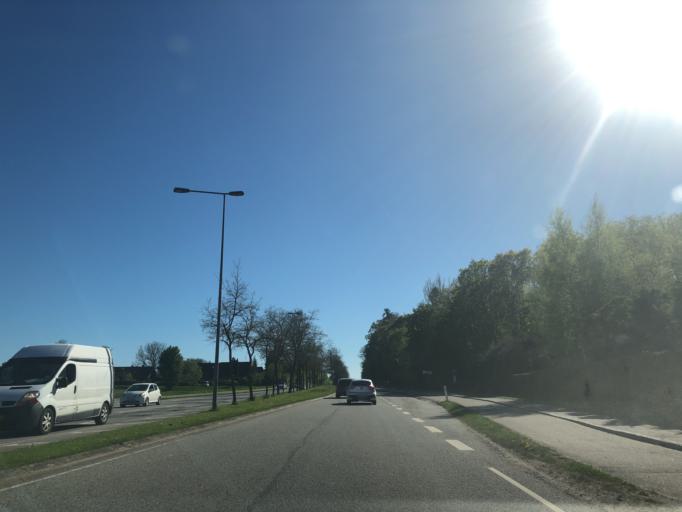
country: DK
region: Zealand
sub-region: Koge Kommune
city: Koge
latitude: 55.4222
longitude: 12.1465
